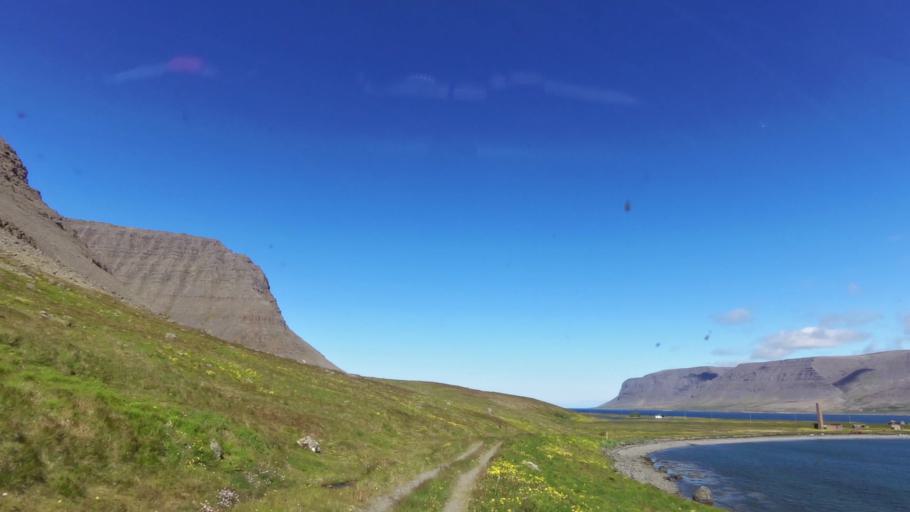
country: IS
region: West
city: Olafsvik
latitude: 65.6360
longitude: -23.9288
